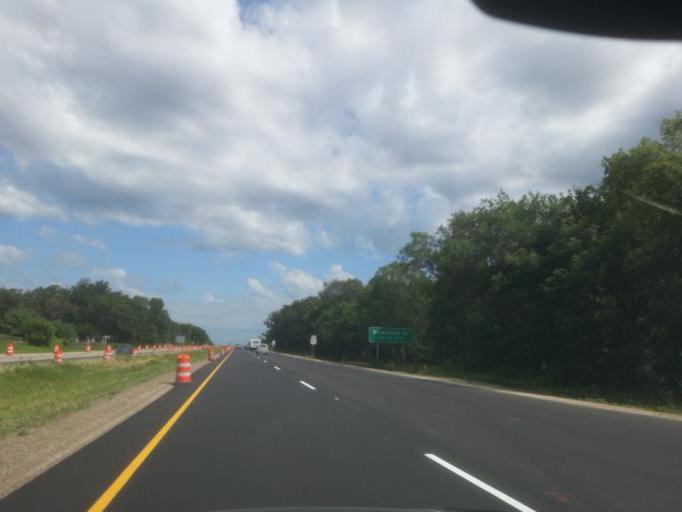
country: US
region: Wisconsin
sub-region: Dane County
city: Monona
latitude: 43.0883
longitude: -89.3126
